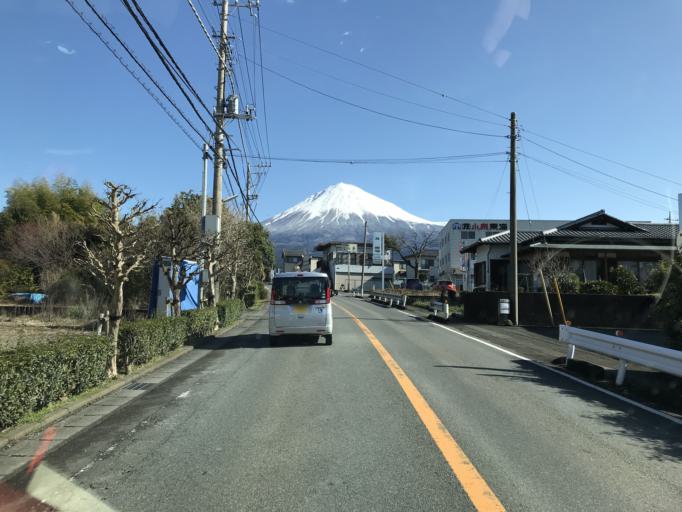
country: JP
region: Shizuoka
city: Fujinomiya
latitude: 35.2485
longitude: 138.6265
